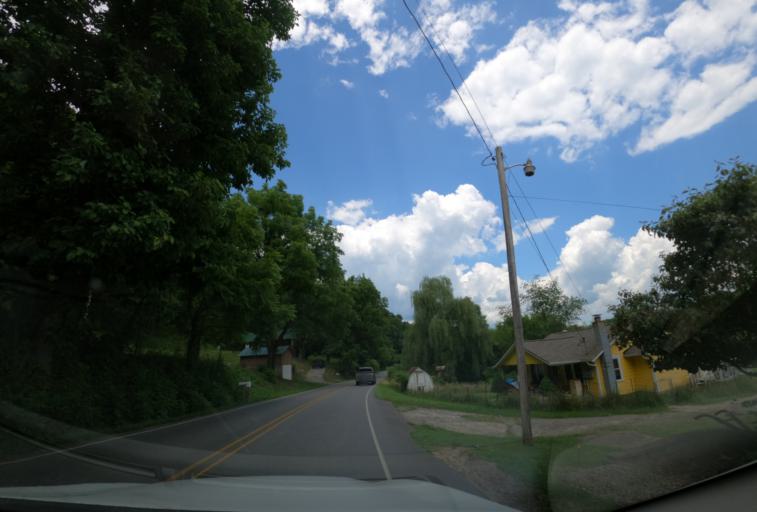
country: US
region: North Carolina
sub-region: Haywood County
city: Clyde
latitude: 35.4558
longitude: -82.9082
